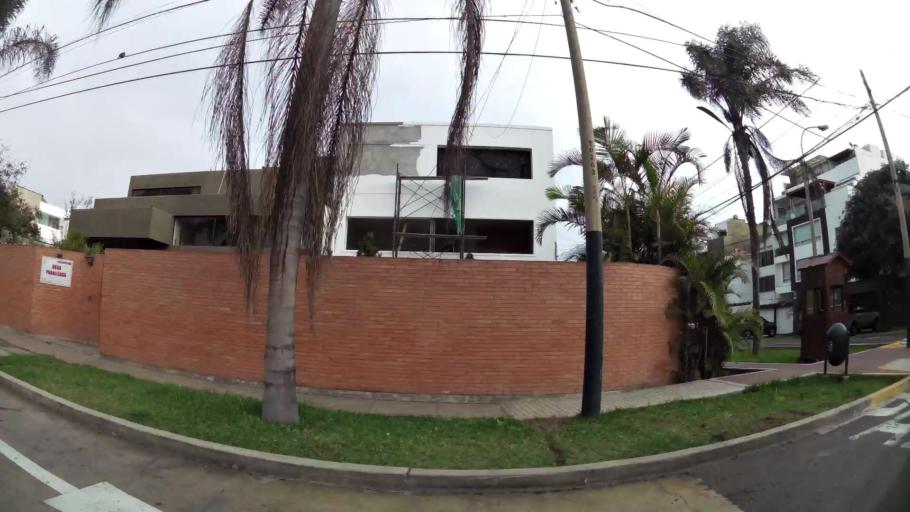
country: PE
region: Lima
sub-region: Lima
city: San Isidro
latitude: -12.0998
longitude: -77.0548
